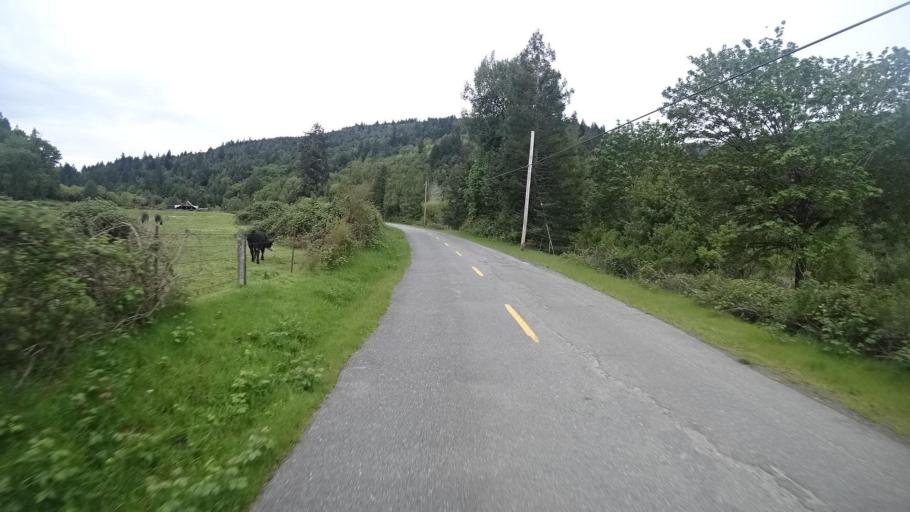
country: US
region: California
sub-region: Humboldt County
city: Blue Lake
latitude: 40.9680
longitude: -123.8415
